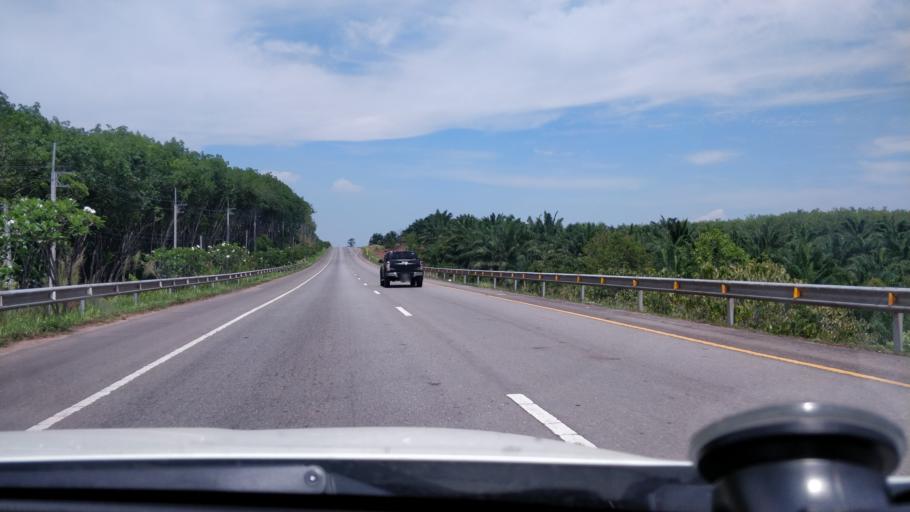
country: TH
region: Surat Thani
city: Chai Buri
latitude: 8.6419
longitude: 99.0599
